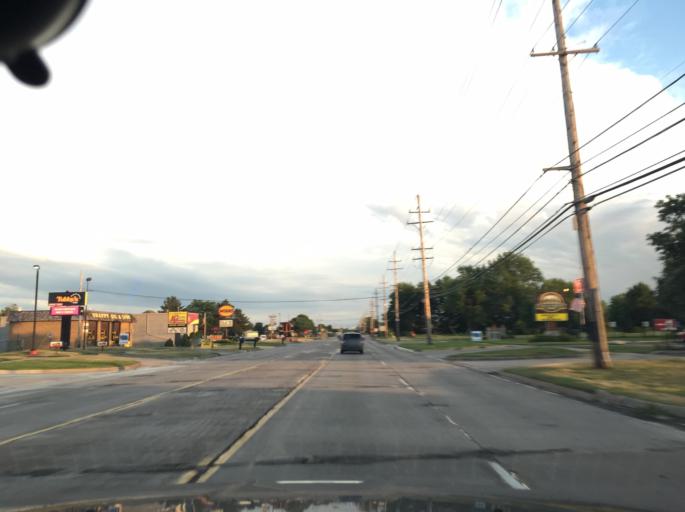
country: US
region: Michigan
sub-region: Macomb County
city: Clinton
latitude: 42.6016
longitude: -82.9525
